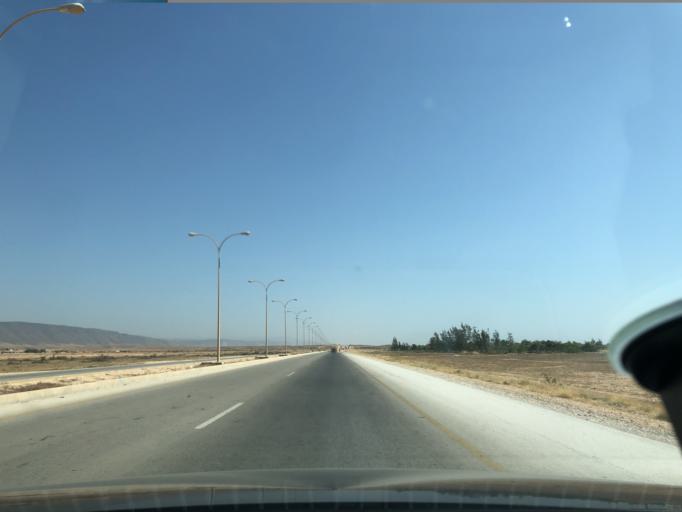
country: OM
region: Zufar
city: Salalah
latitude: 17.0525
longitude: 54.2912
